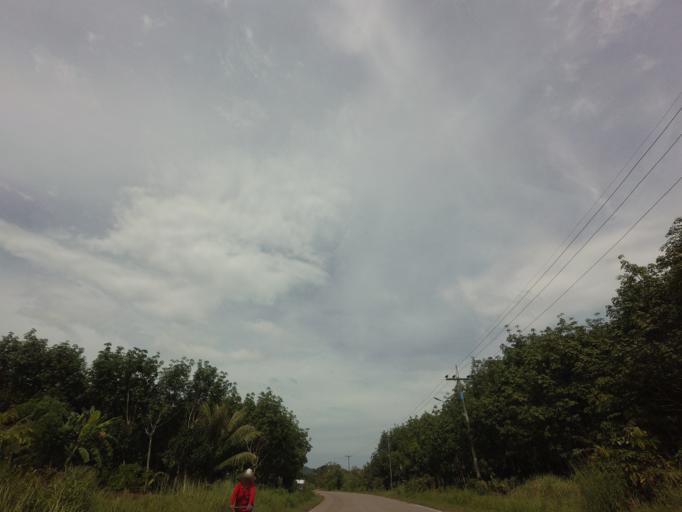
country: TH
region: Rayong
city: Klaeng
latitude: 12.6855
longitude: 101.5405
